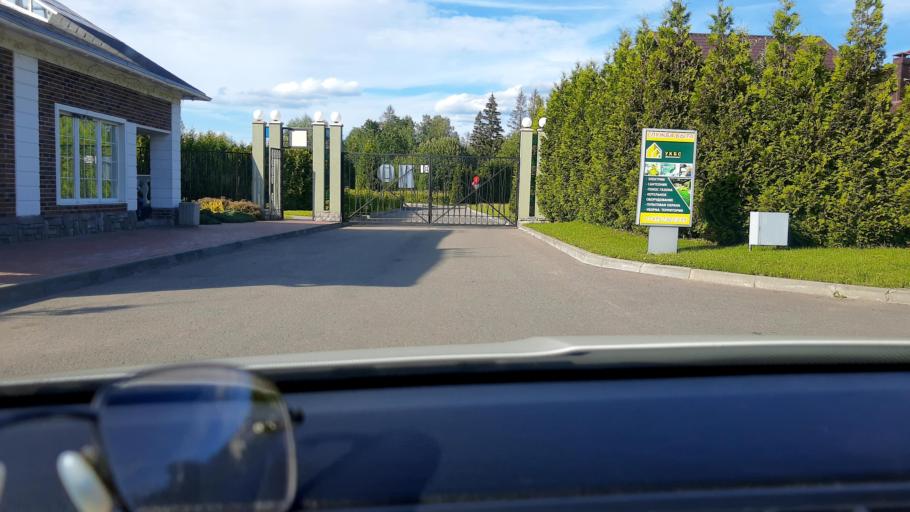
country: RU
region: Moskovskaya
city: Nazar'yevo
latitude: 55.6910
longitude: 37.0395
